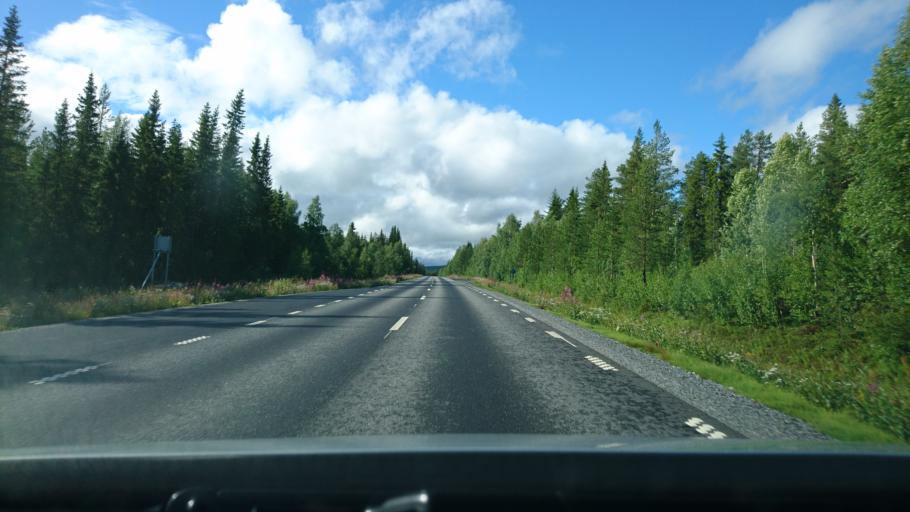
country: SE
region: Vaesterbotten
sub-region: Vilhelmina Kommun
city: Vilhelmina
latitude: 64.6912
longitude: 16.7226
